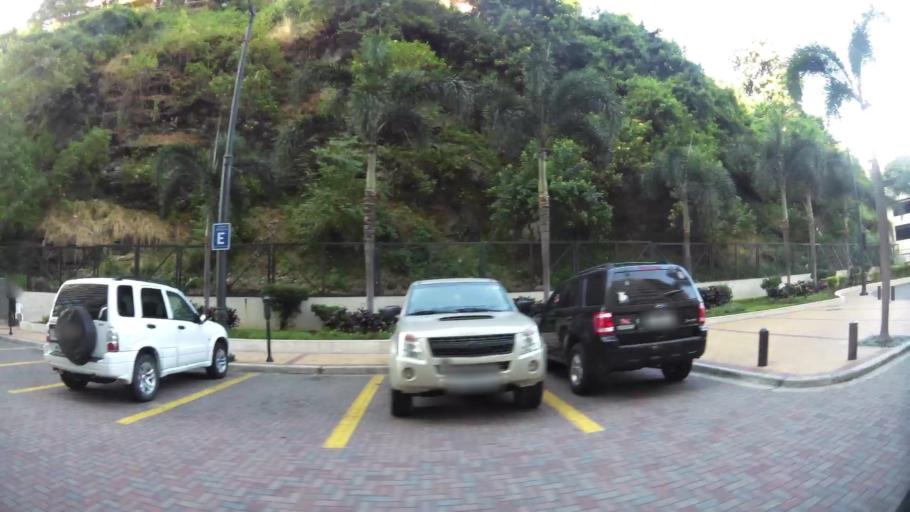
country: EC
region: Guayas
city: Eloy Alfaro
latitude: -2.1798
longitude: -79.8754
